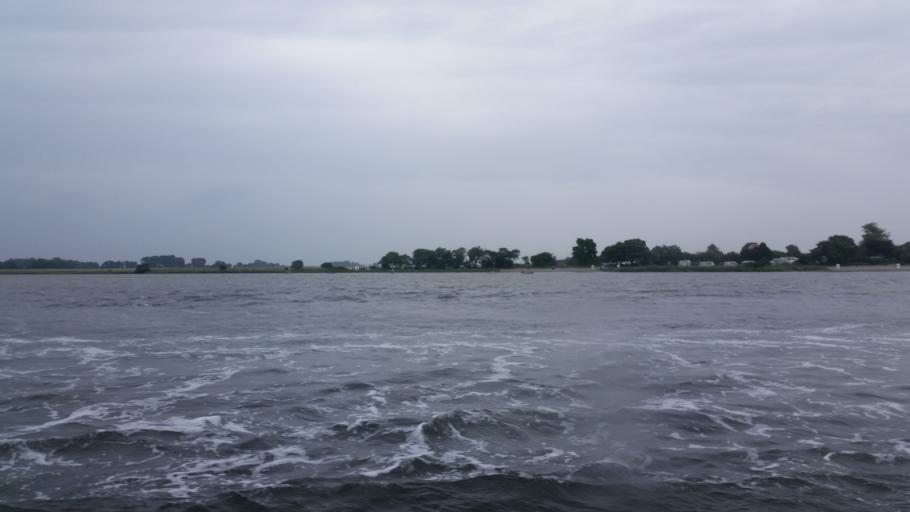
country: DE
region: Mecklenburg-Vorpommern
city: Hiddensee
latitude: 54.5166
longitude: 13.1582
